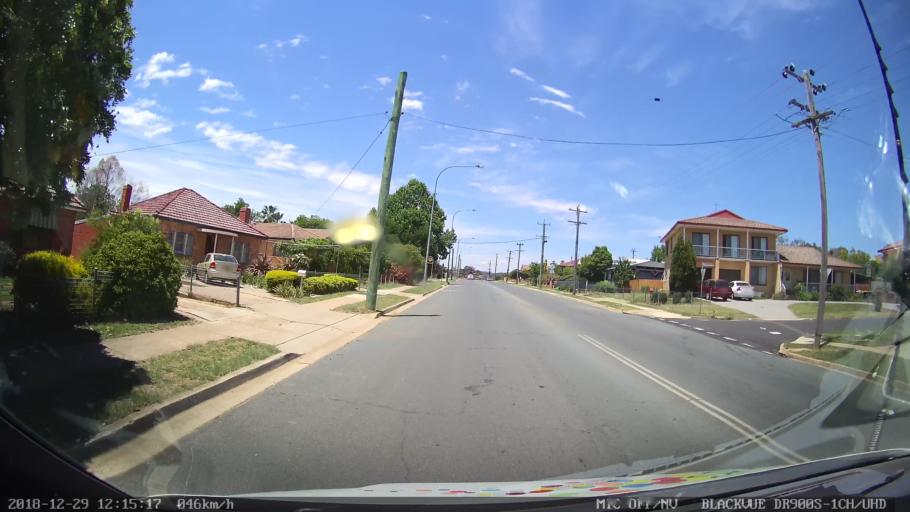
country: AU
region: New South Wales
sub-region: Queanbeyan
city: Queanbeyan
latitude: -35.3608
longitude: 149.2335
